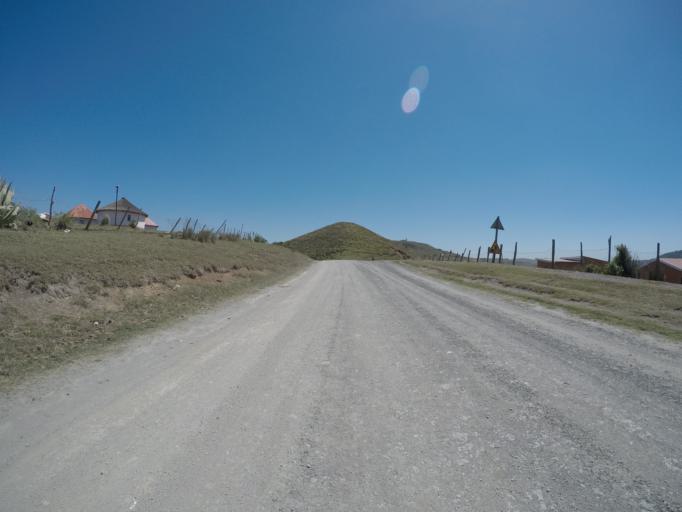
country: ZA
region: Eastern Cape
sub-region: OR Tambo District Municipality
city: Libode
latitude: -32.0164
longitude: 29.0782
